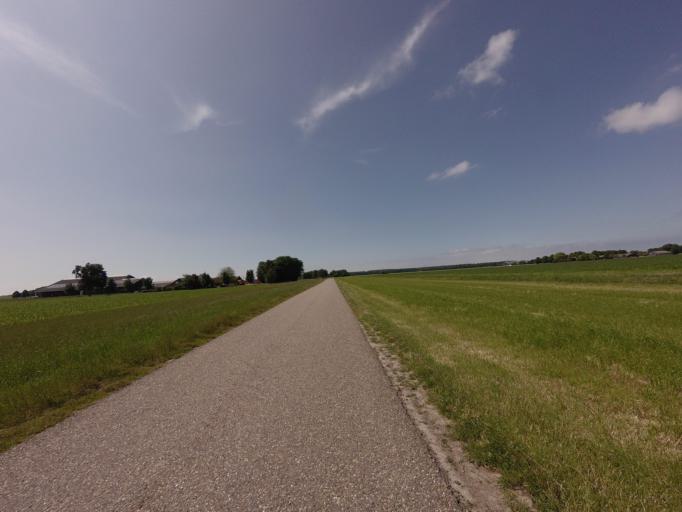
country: NL
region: Flevoland
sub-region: Gemeente Lelystad
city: Lelystad
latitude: 52.4385
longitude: 5.4636
